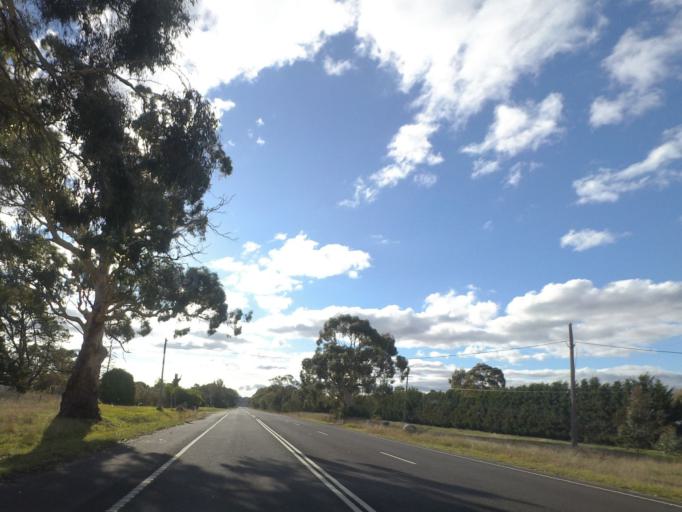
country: AU
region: Victoria
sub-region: Mount Alexander
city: Castlemaine
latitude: -37.1524
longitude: 144.3531
